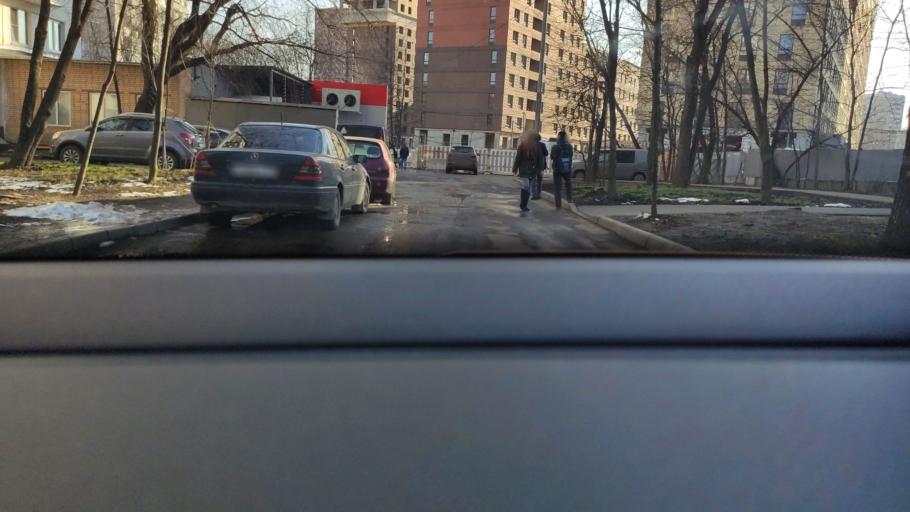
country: RU
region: Moskovskaya
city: Bol'shaya Setun'
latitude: 55.7474
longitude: 37.4087
